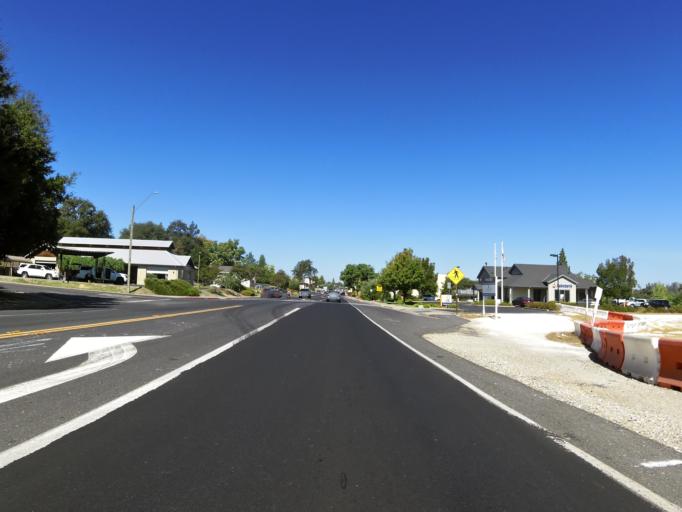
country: US
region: California
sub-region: Calaveras County
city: Angels Camp
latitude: 38.0771
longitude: -120.5498
